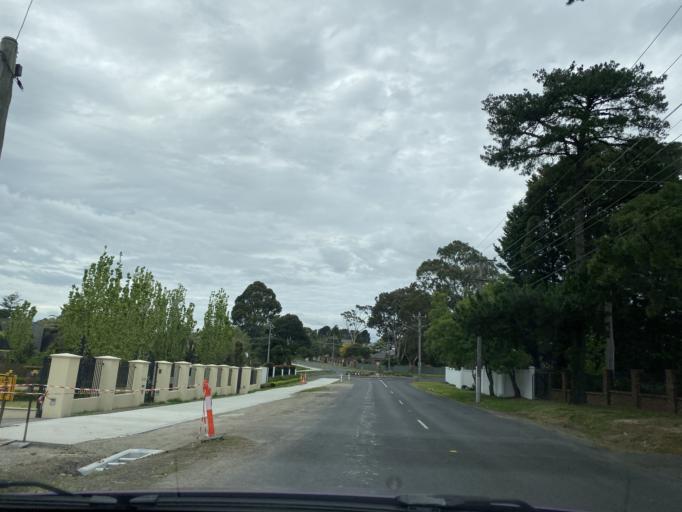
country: AU
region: Victoria
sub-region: Manningham
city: Doncaster East
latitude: -37.7650
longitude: 145.1407
